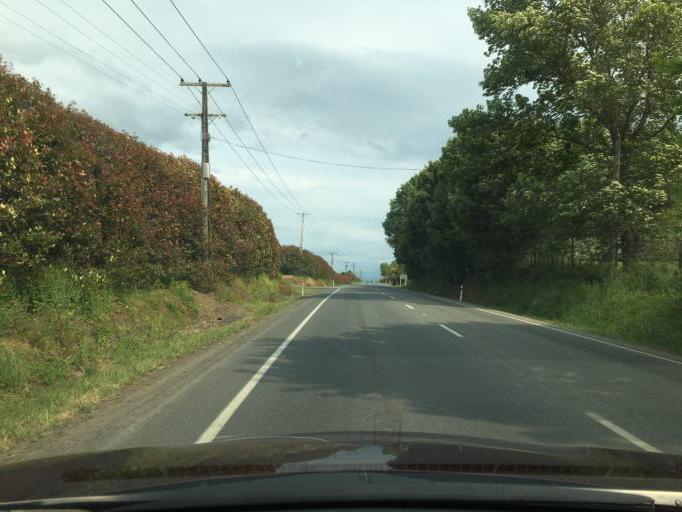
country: NZ
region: Waikato
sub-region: Waipa District
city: Cambridge
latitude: -38.0092
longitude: 175.3538
